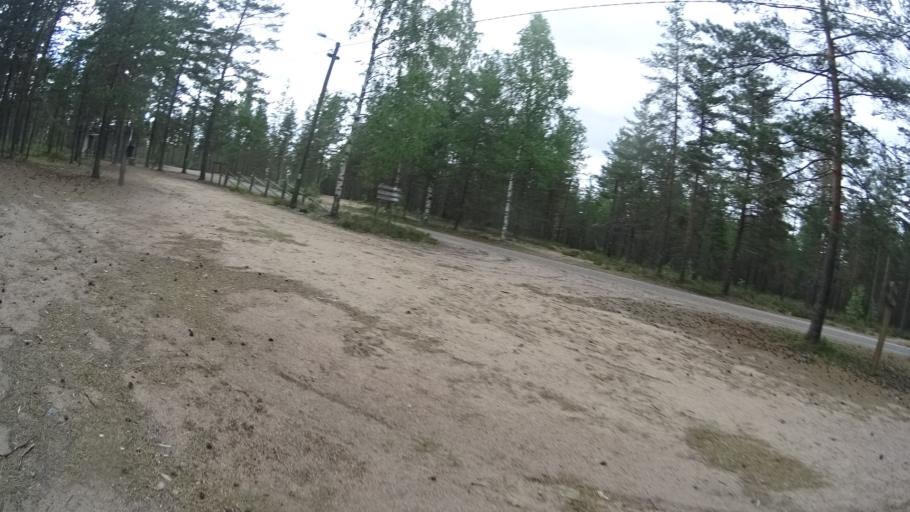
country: FI
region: Satakunta
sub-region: Pohjois-Satakunta
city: Jaemijaervi
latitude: 61.7755
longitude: 22.7313
